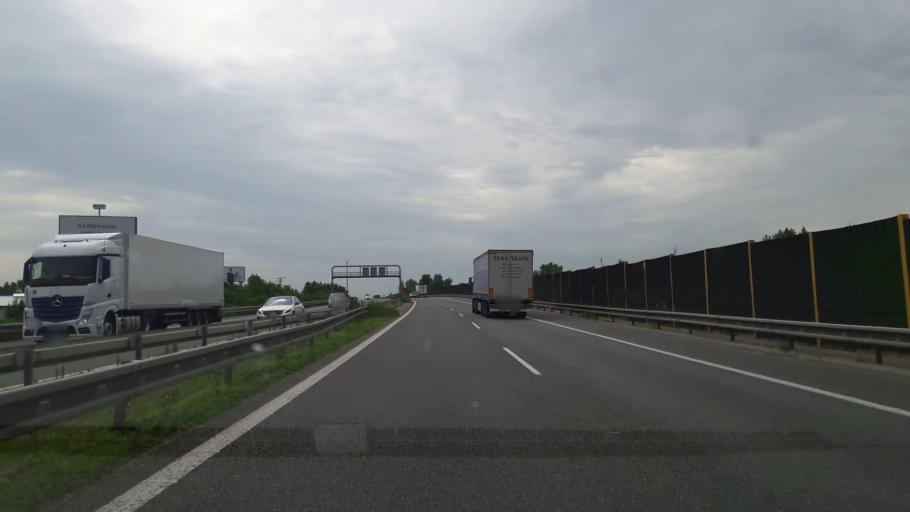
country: AT
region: Burgenland
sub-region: Politischer Bezirk Neusiedl am See
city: Kittsee
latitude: 48.1103
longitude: 17.0851
